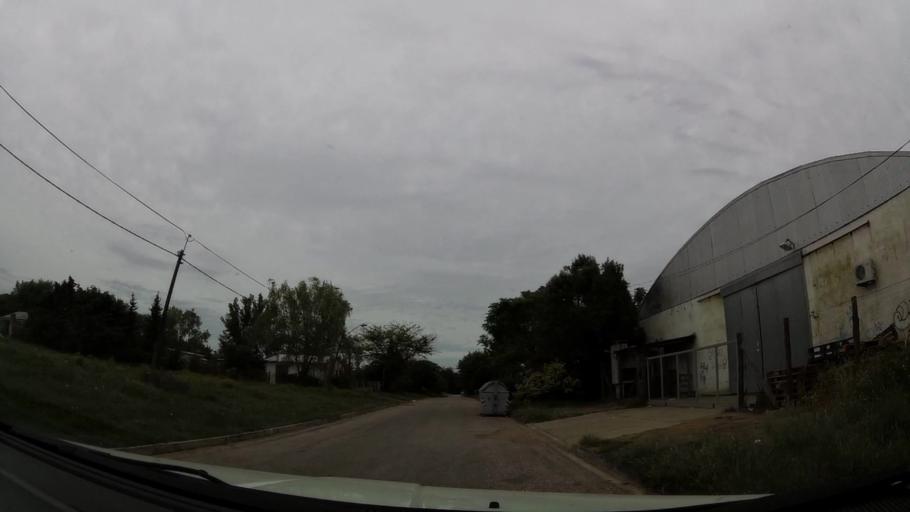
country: UY
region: Maldonado
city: Maldonado
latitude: -34.8803
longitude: -54.9851
